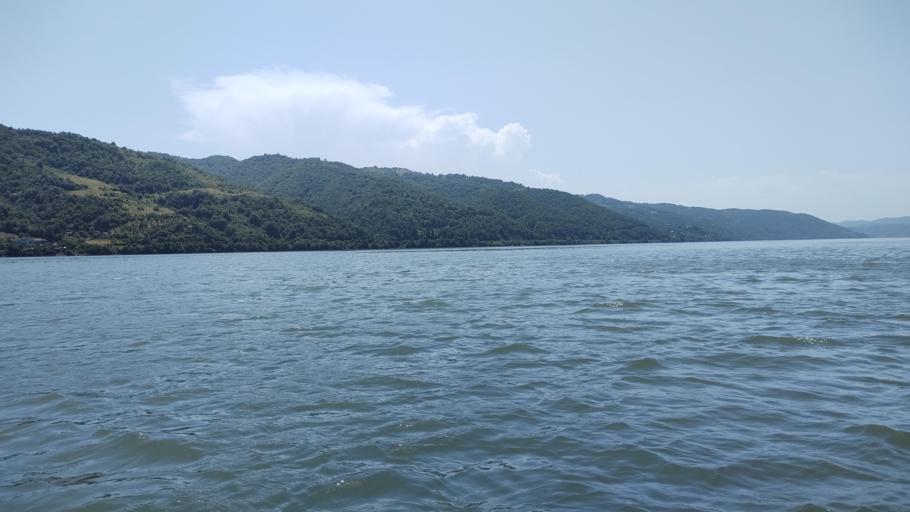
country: RO
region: Mehedinti
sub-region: Comuna Svinita
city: Svinita
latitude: 44.5274
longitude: 22.2059
